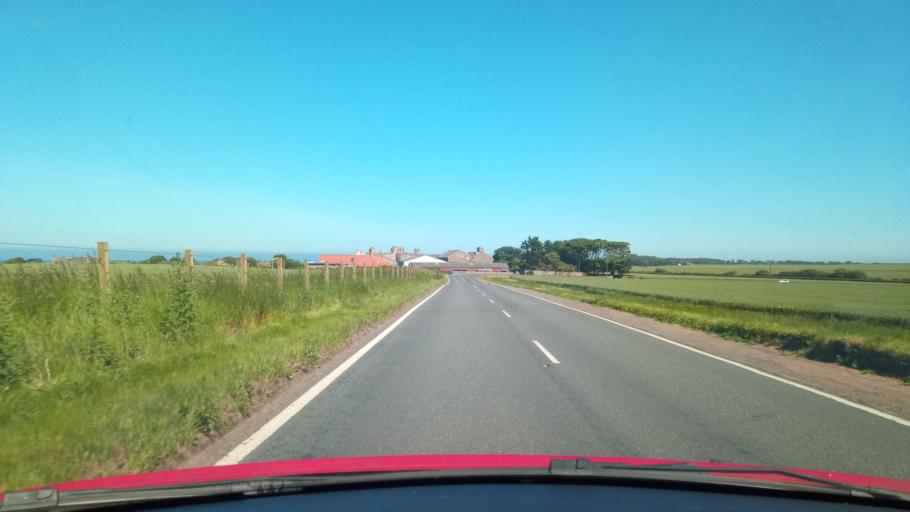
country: GB
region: Scotland
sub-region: East Lothian
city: North Berwick
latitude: 56.0565
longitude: -2.6632
